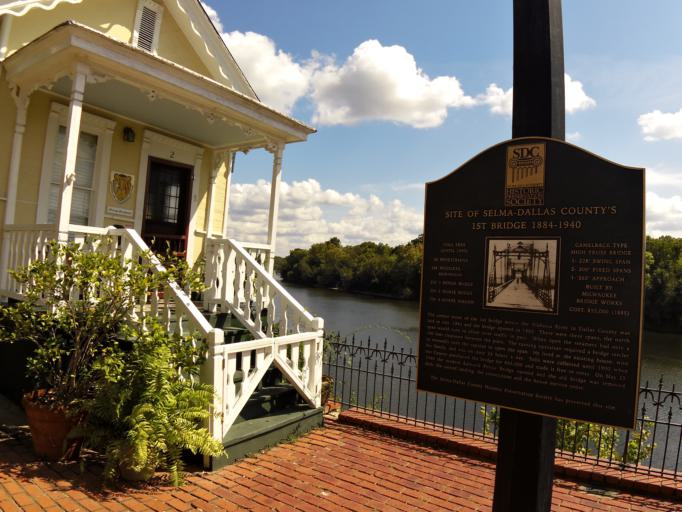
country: US
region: Alabama
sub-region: Dallas County
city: Selma
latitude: 32.4065
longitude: -87.0179
